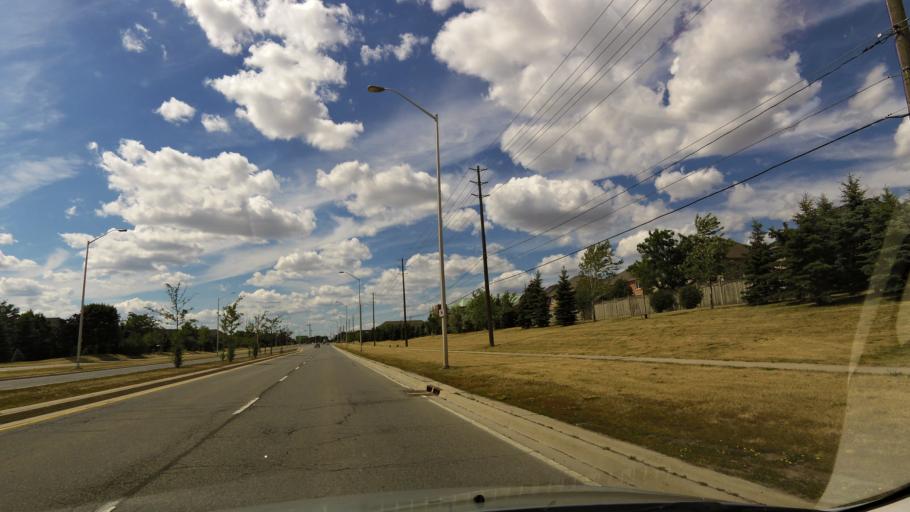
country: CA
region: Ontario
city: Oakville
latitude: 43.4253
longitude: -79.7621
